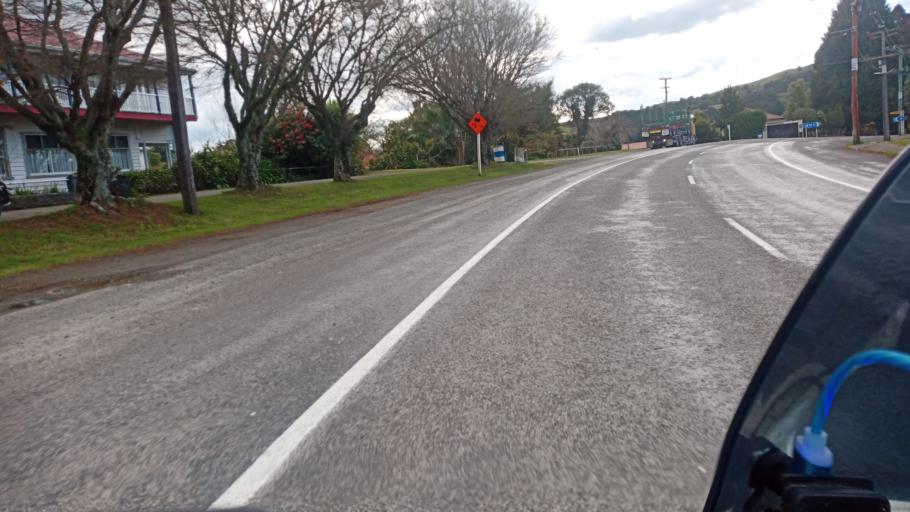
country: NZ
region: Gisborne
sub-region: Gisborne District
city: Gisborne
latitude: -38.0569
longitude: 178.3052
